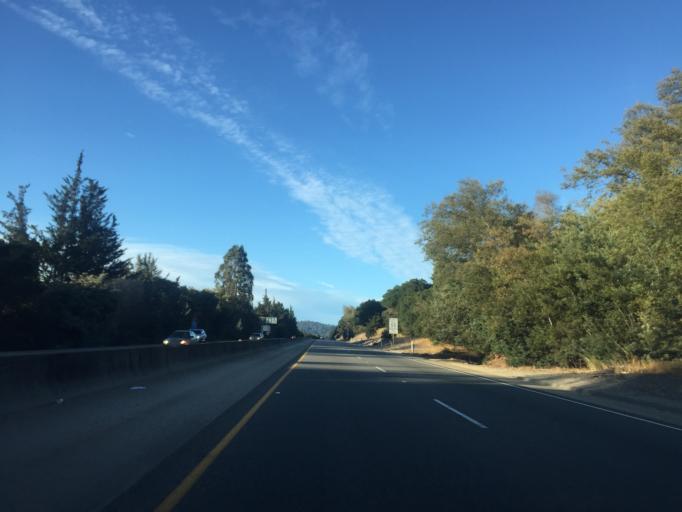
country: US
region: California
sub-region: Santa Cruz County
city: Scotts Valley
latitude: 37.0384
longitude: -122.0173
